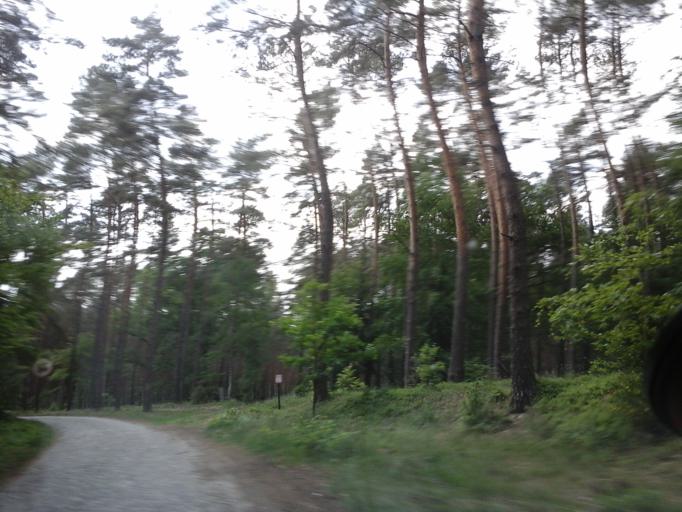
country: PL
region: West Pomeranian Voivodeship
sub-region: Powiat choszczenski
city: Drawno
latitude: 53.1130
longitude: 15.7858
